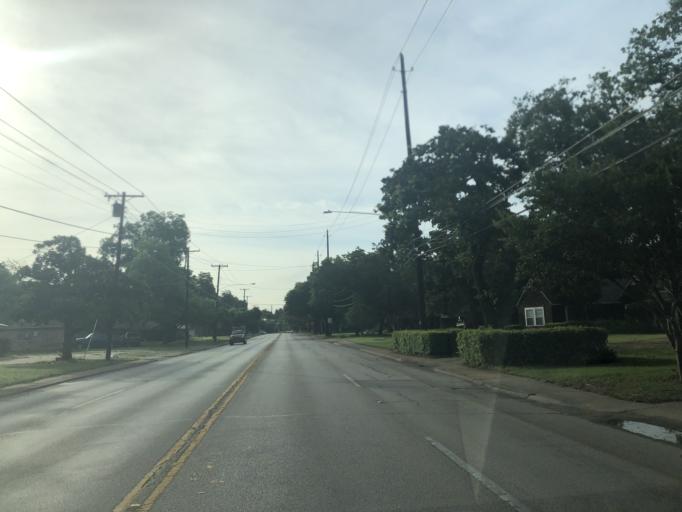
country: US
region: Texas
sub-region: Dallas County
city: Irving
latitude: 32.8013
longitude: -96.9831
